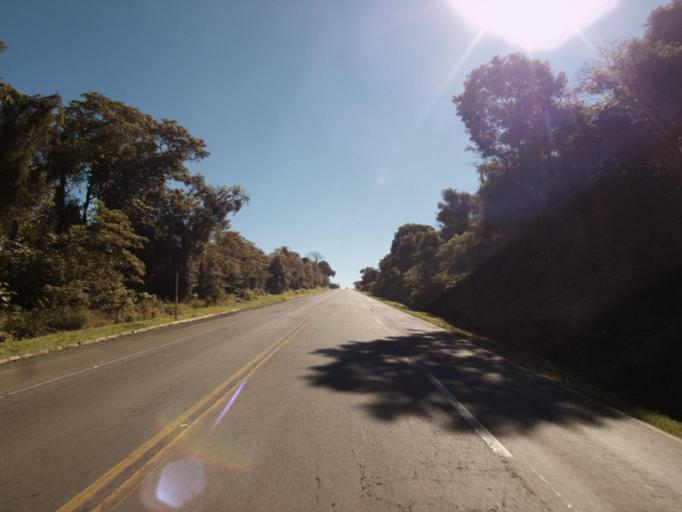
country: BR
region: Rio Grande do Sul
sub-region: Frederico Westphalen
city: Frederico Westphalen
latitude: -26.8368
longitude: -53.1755
